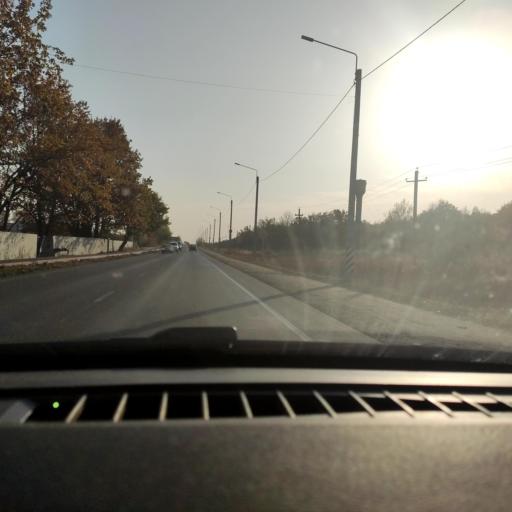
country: RU
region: Voronezj
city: Semiluki
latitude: 51.7323
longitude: 39.0403
